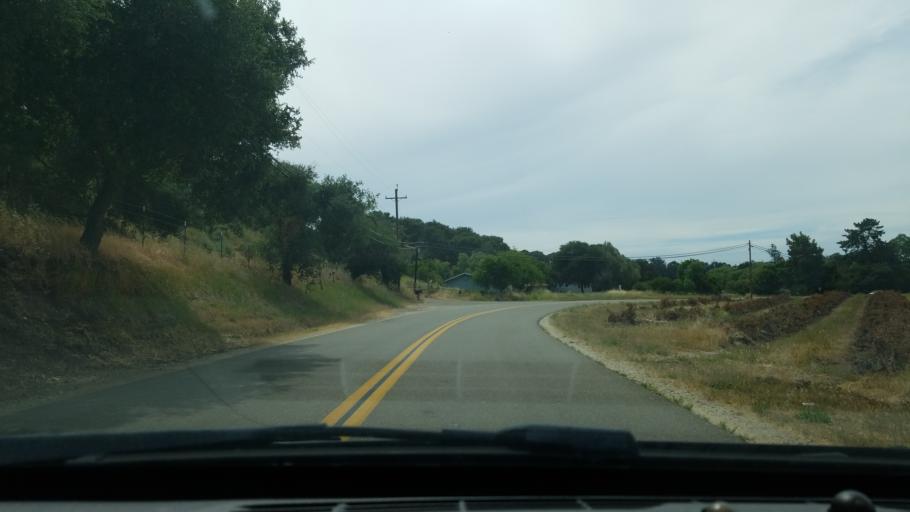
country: US
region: California
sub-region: Santa Barbara County
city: Los Alamos
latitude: 34.8536
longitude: -120.2632
